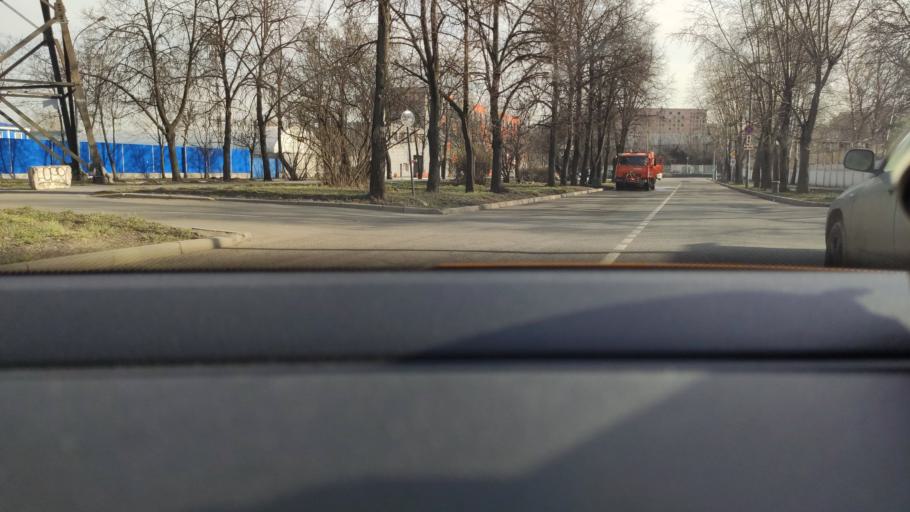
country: RU
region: Moscow
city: Mar'ina Roshcha
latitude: 55.8088
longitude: 37.5950
